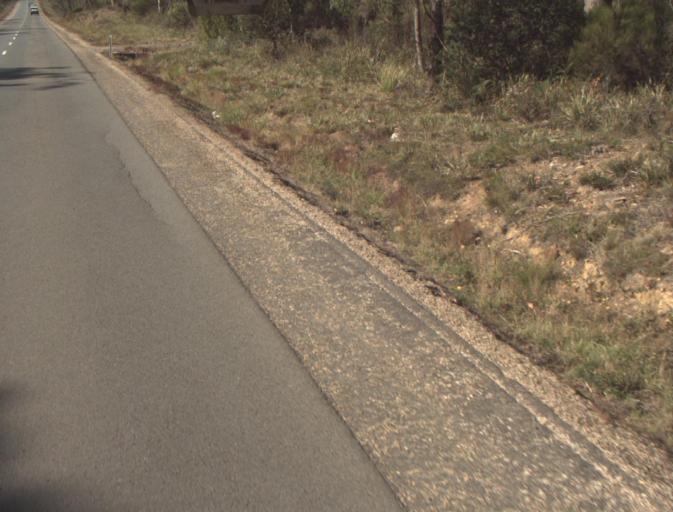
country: AU
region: Tasmania
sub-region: Launceston
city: Mayfield
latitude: -41.3176
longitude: 147.1920
